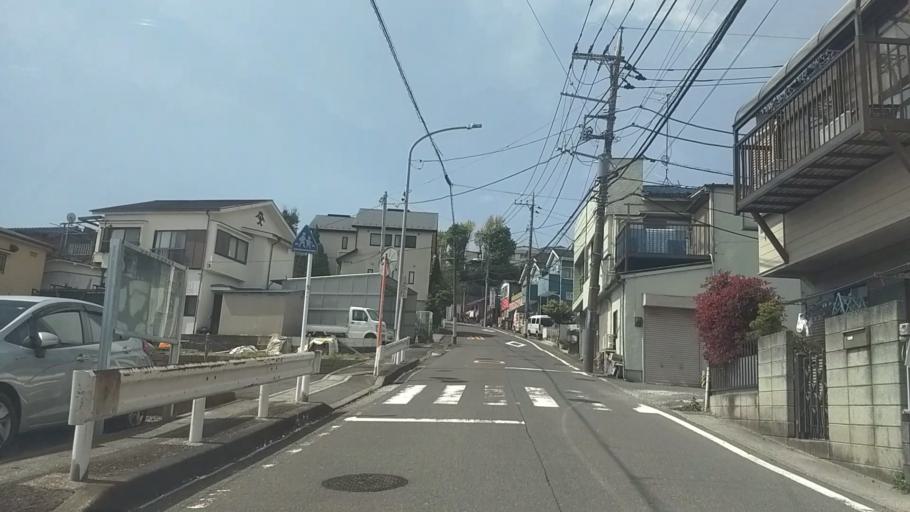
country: JP
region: Kanagawa
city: Yokohama
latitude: 35.3943
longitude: 139.5943
